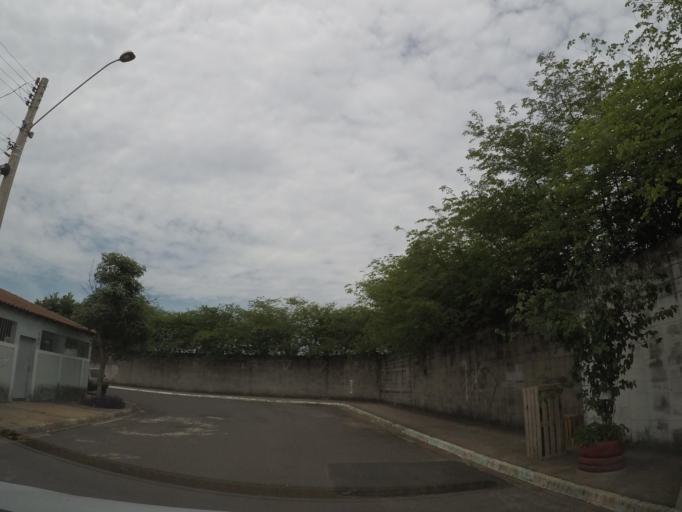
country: BR
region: Sao Paulo
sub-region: Hortolandia
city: Hortolandia
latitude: -22.8341
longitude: -47.1927
